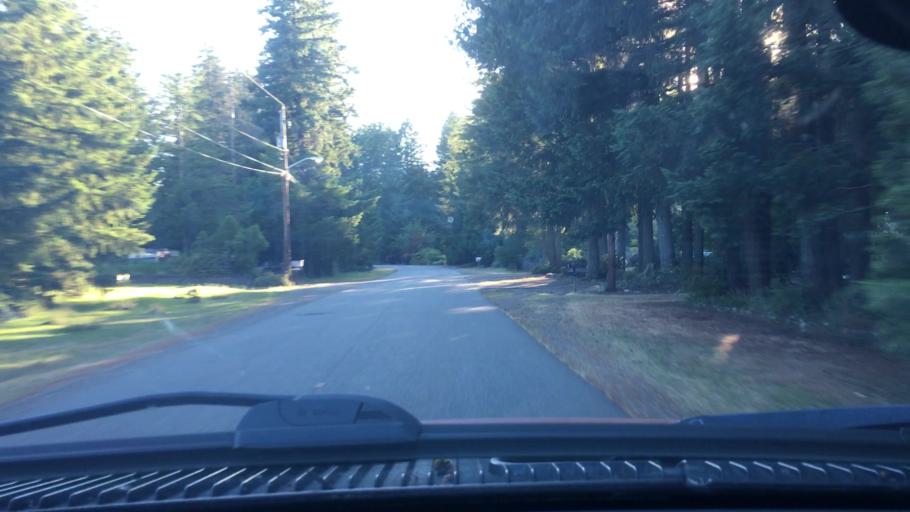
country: US
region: Washington
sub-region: King County
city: Lake Morton-Berrydale
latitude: 47.3473
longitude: -122.0794
